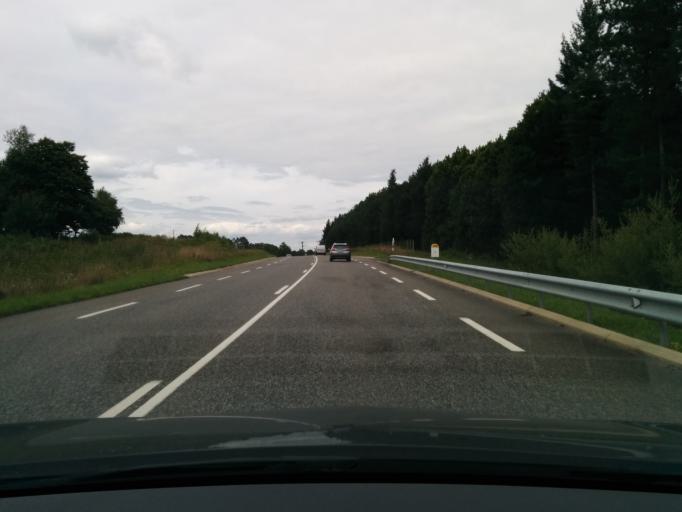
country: FR
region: Midi-Pyrenees
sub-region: Departement des Hautes-Pyrenees
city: La Barthe-de-Neste
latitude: 43.0730
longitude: 0.3616
